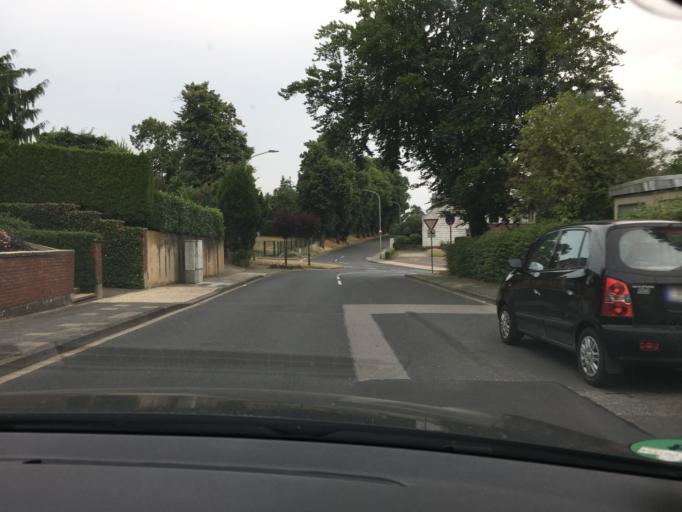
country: DE
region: North Rhine-Westphalia
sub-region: Regierungsbezirk Koln
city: Merzenich
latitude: 50.8263
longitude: 6.5314
